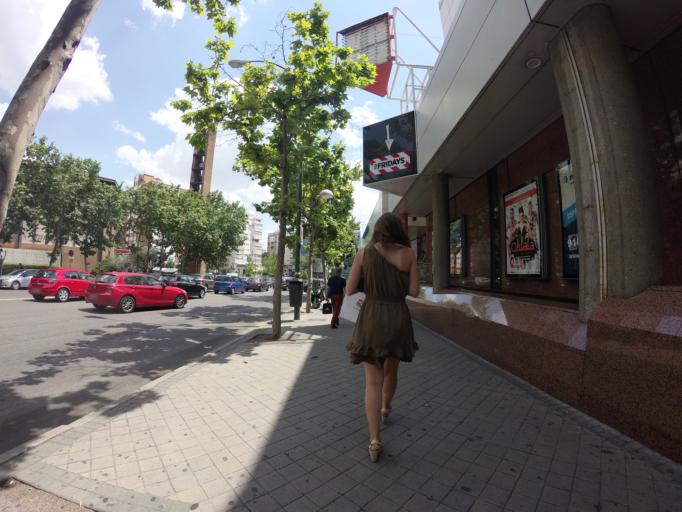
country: ES
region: Madrid
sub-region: Provincia de Madrid
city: Chamartin
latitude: 40.4526
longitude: -3.6864
